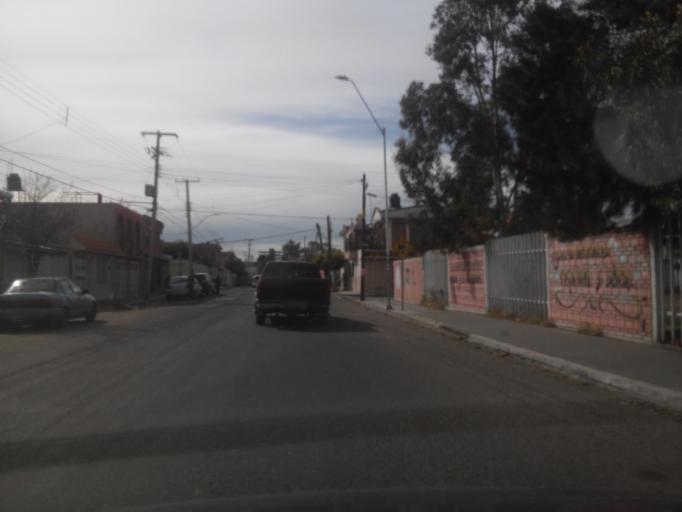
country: MX
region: Durango
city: Victoria de Durango
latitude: 24.0080
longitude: -104.6557
